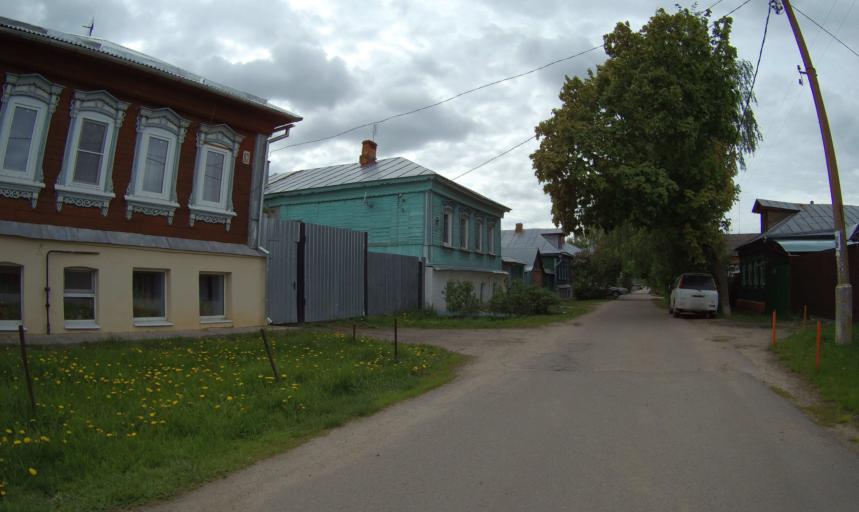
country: RU
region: Moskovskaya
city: Kolomna
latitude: 55.0984
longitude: 38.7499
